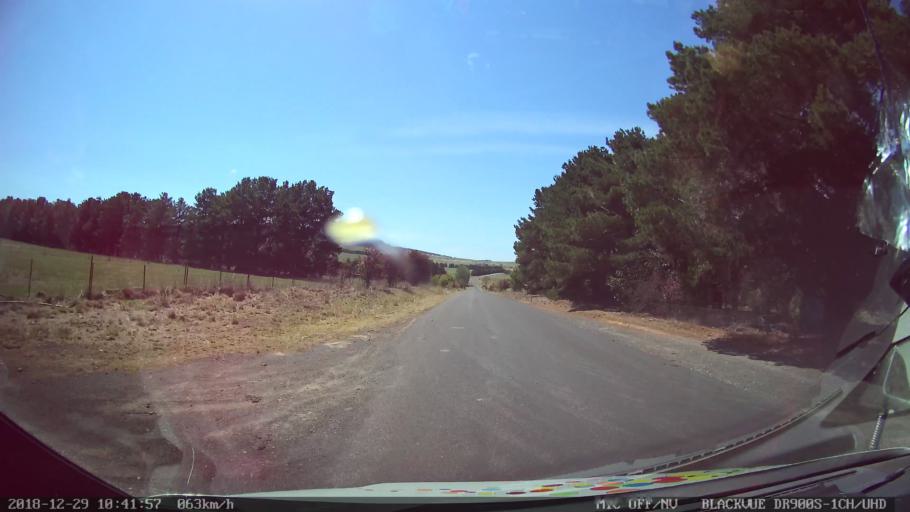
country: AU
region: New South Wales
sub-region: Palerang
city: Bungendore
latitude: -35.0295
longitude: 149.5251
